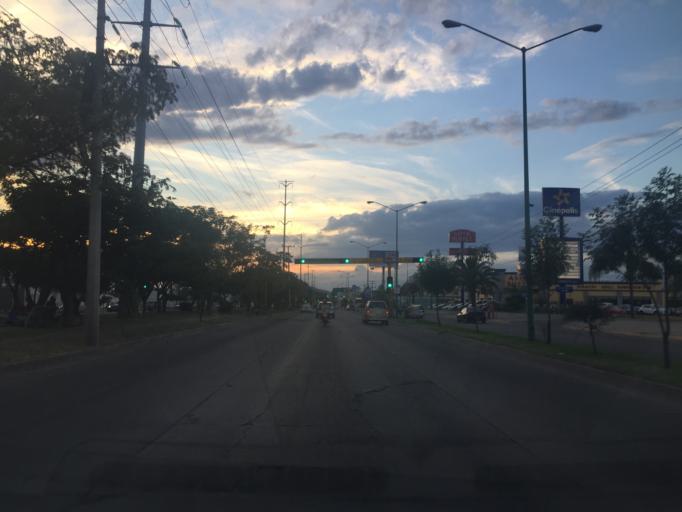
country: MX
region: Guanajuato
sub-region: Leon
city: Medina
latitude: 21.1456
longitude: -101.6480
